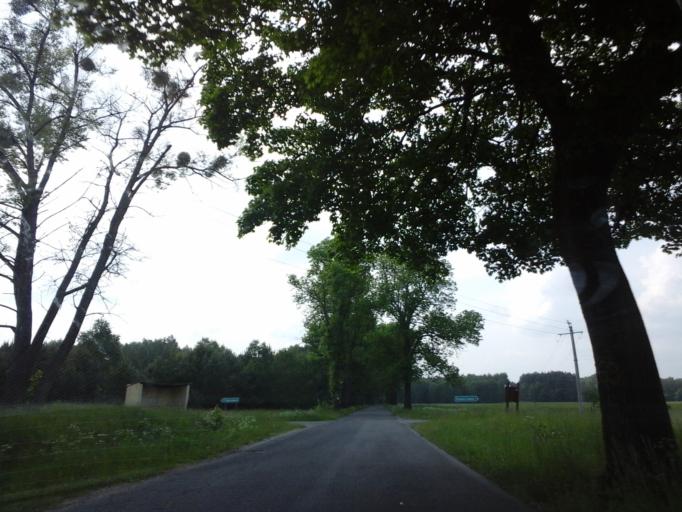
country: PL
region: West Pomeranian Voivodeship
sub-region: Powiat choszczenski
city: Drawno
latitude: 53.1946
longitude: 15.8375
